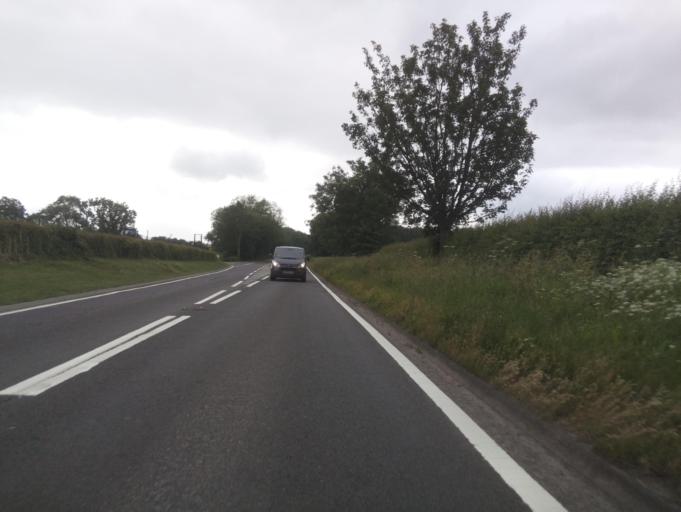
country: GB
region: England
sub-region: Derbyshire
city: Rodsley
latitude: 52.9201
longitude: -1.7607
